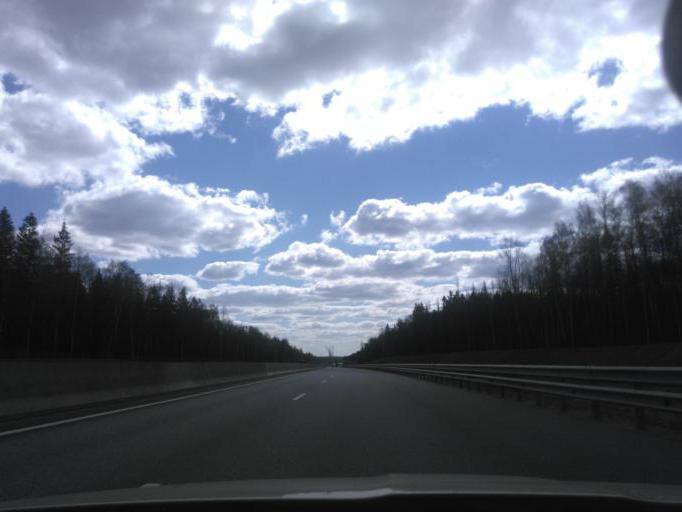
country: RU
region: Moskovskaya
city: Mendeleyevo
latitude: 56.0698
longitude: 37.2222
